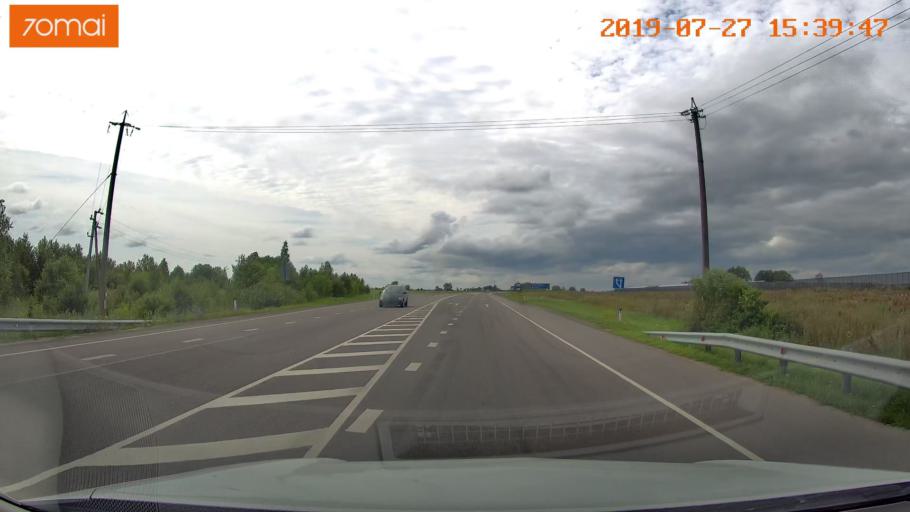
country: RU
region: Kaliningrad
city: Gusev
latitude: 54.6050
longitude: 22.2780
